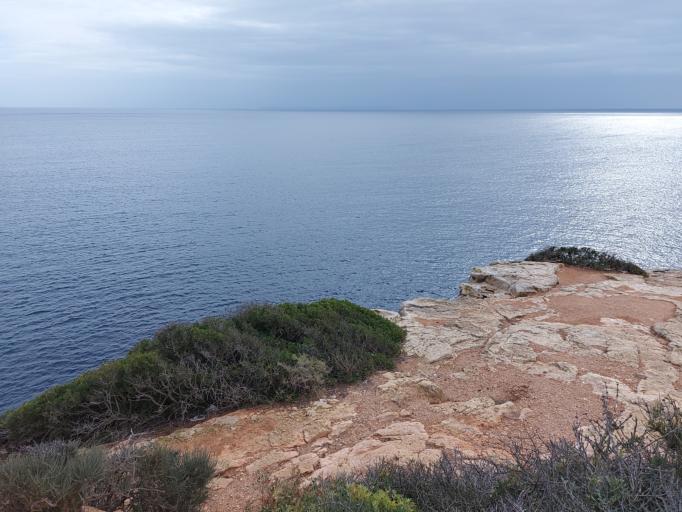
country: ES
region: Balearic Islands
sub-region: Illes Balears
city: Llucmajor
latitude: 39.3614
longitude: 2.8354
